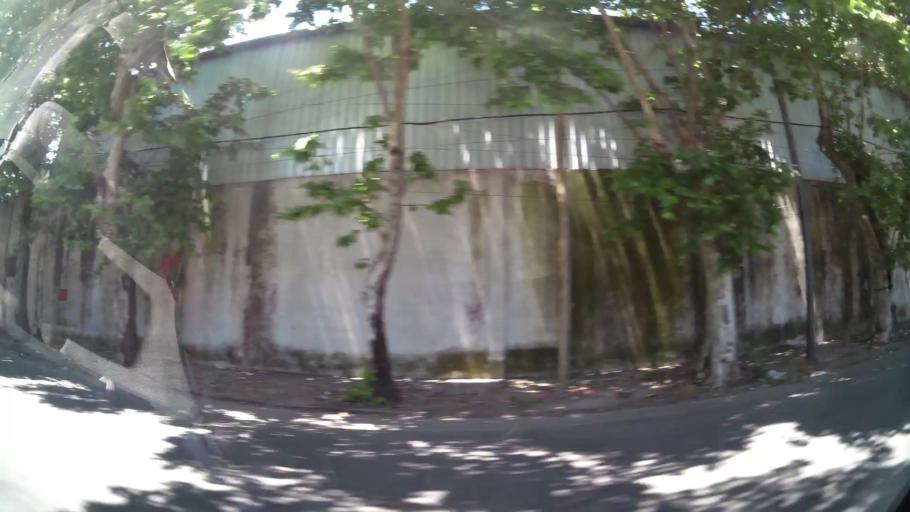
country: AR
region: Buenos Aires
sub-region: Partido de Avellaneda
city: Avellaneda
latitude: -34.6601
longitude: -58.3915
